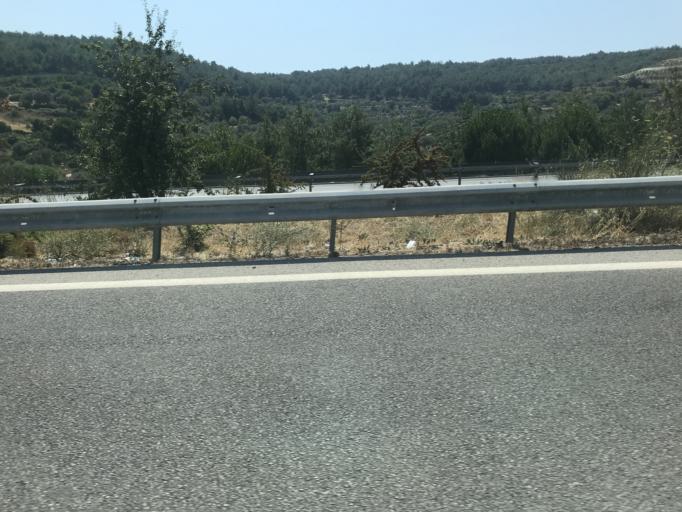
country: TR
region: Izmir
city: Urla
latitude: 38.3223
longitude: 26.8001
